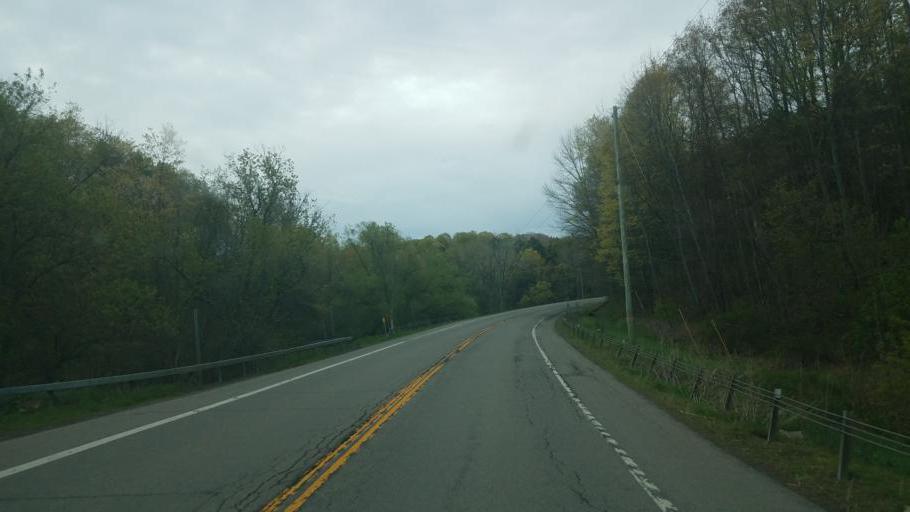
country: US
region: New York
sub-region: Steuben County
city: Canisteo
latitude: 42.1725
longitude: -77.5281
